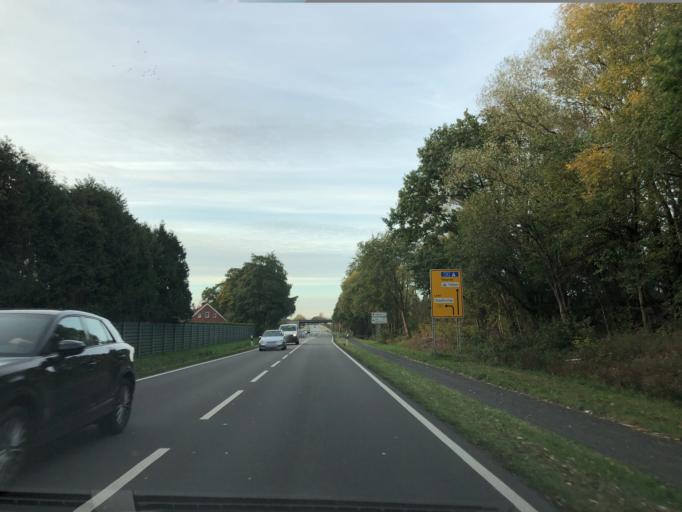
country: DE
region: Lower Saxony
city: Papenburg
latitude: 53.0693
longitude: 7.3914
